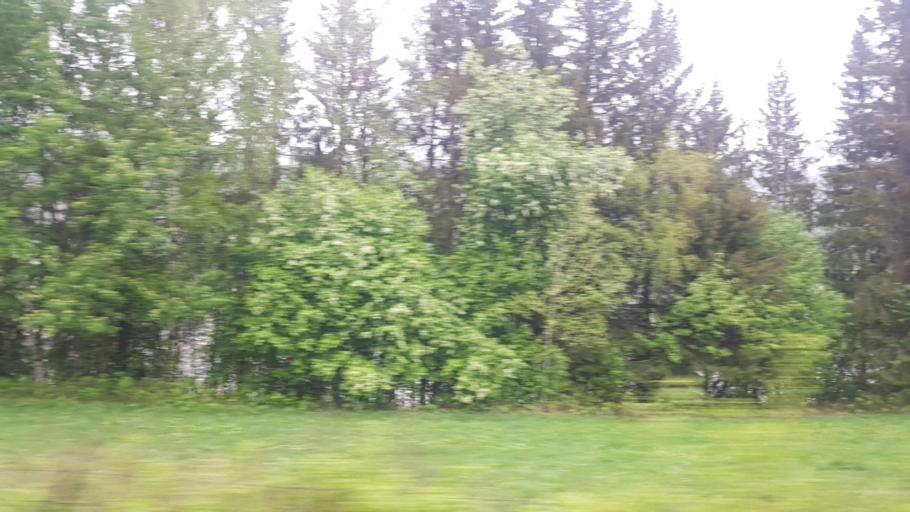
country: NO
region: Oppland
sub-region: Oyer
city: Tretten
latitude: 61.3916
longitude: 10.2535
